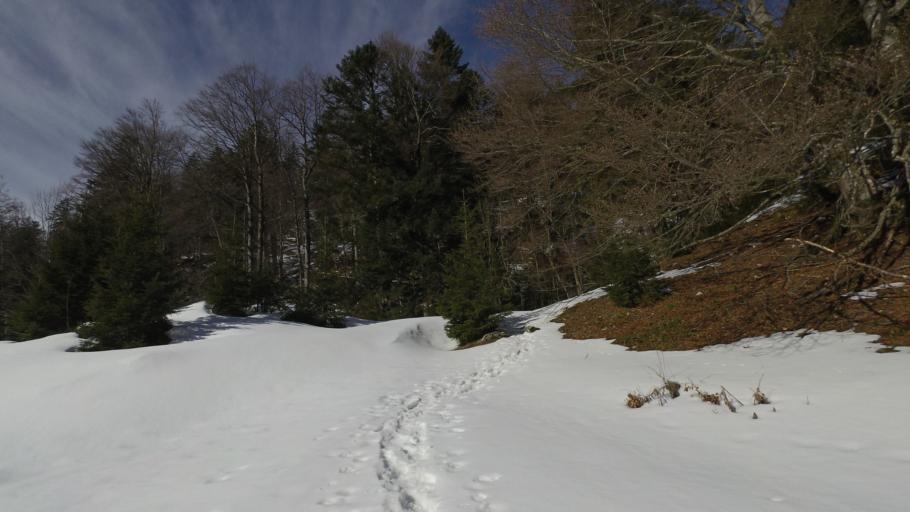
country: DE
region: Bavaria
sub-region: Upper Bavaria
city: Reit im Winkl
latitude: 47.6919
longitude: 12.4474
